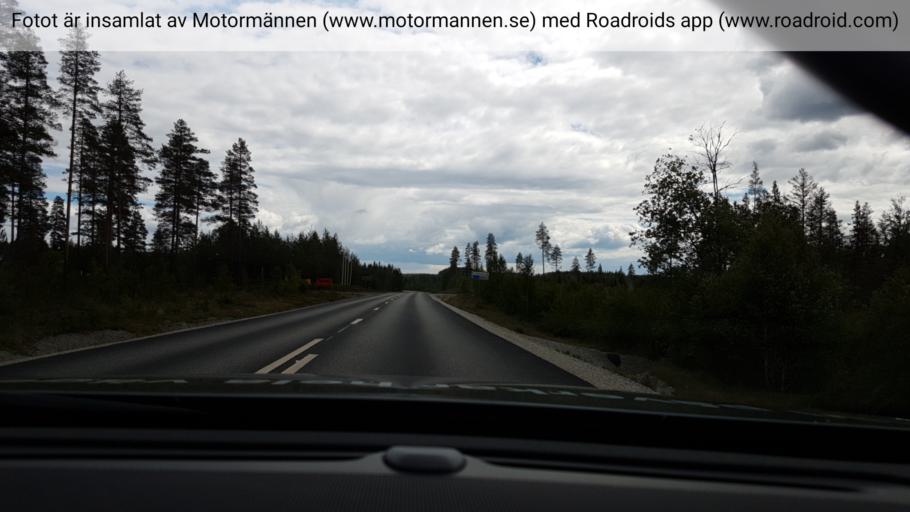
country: SE
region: Vaesterbotten
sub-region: Vindelns Kommun
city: Vindeln
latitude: 64.0596
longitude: 19.6451
